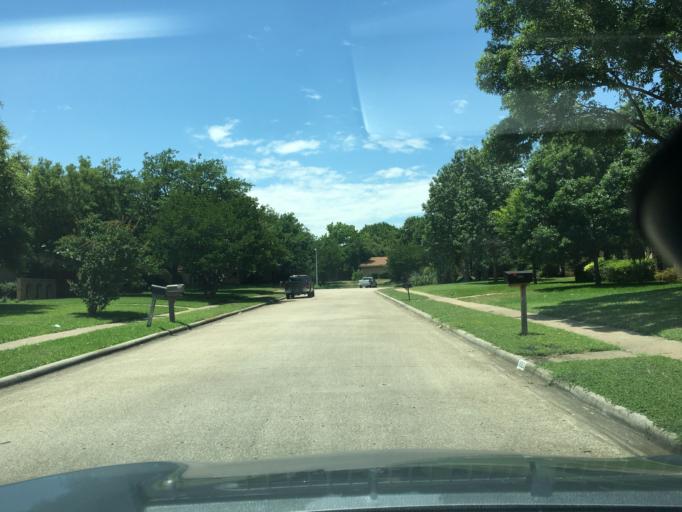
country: US
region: Texas
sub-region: Dallas County
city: Richardson
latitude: 32.9327
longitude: -96.6954
